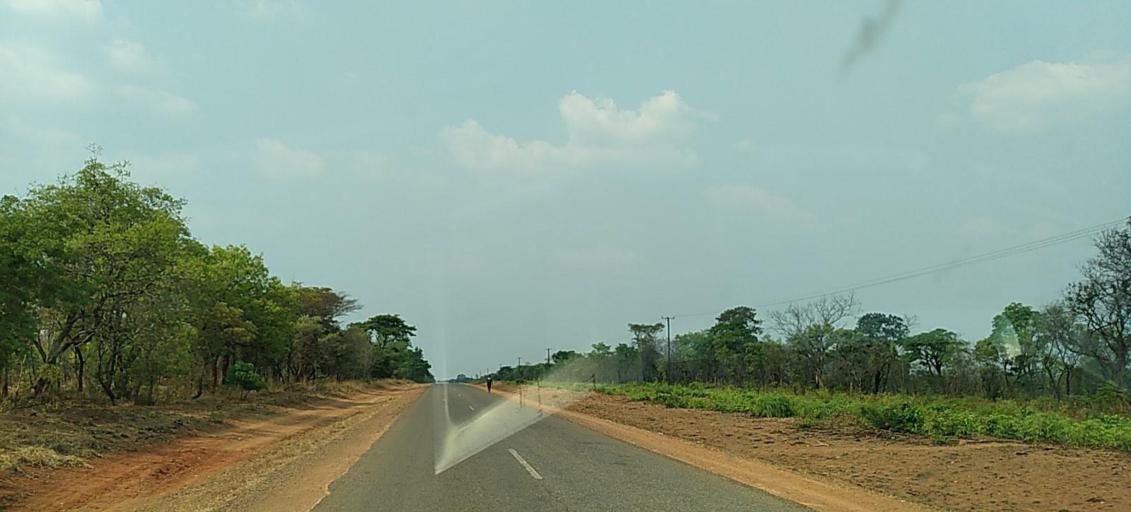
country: ZM
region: North-Western
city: Kabompo
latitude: -13.5725
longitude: 24.2435
